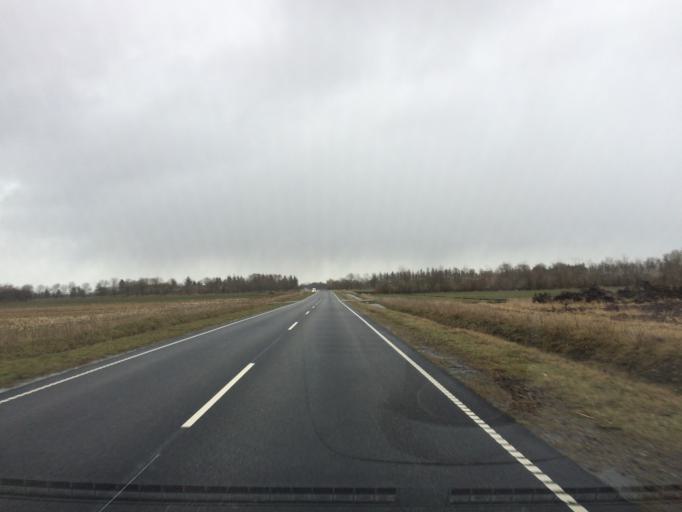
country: DK
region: Central Jutland
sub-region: Herning Kommune
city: Vildbjerg
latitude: 56.1826
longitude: 8.6819
